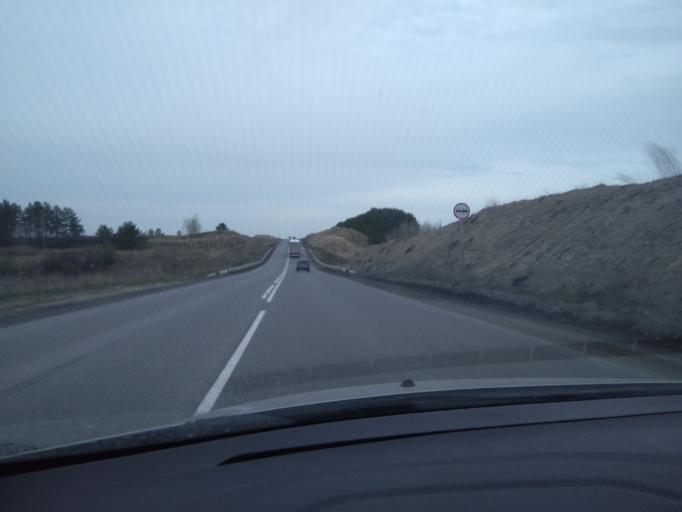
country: RU
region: Sverdlovsk
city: Kamyshlov
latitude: 56.8705
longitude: 62.9381
